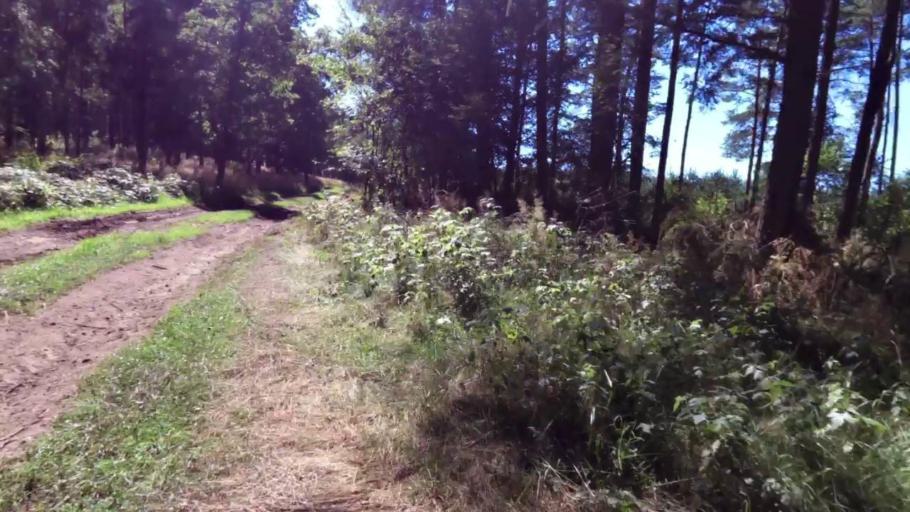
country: PL
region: West Pomeranian Voivodeship
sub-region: Powiat szczecinecki
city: Bialy Bor
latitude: 53.8524
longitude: 16.7611
